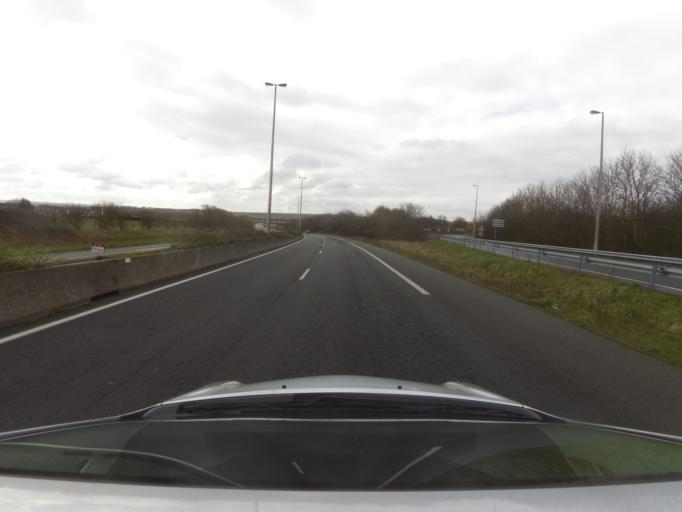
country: FR
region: Nord-Pas-de-Calais
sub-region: Departement du Pas-de-Calais
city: Ferques
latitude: 50.8789
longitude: 1.7490
